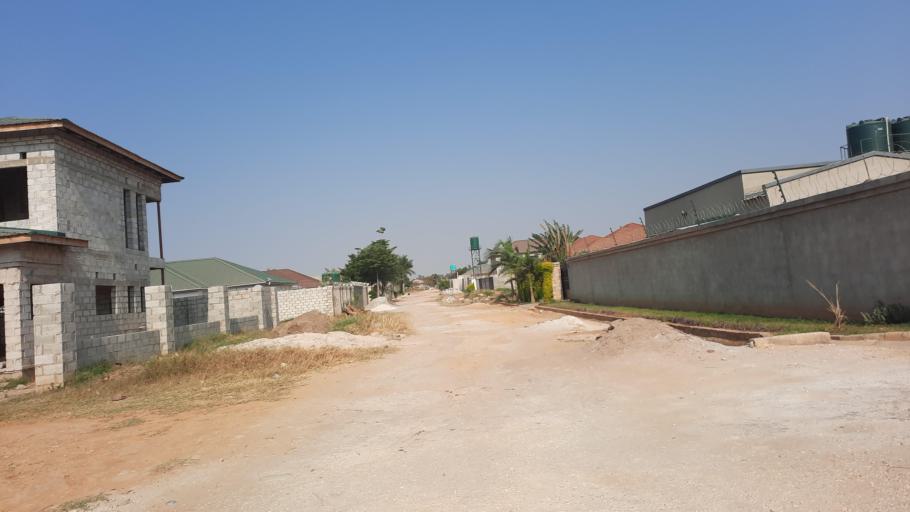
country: ZM
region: Lusaka
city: Lusaka
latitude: -15.3929
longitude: 28.3896
